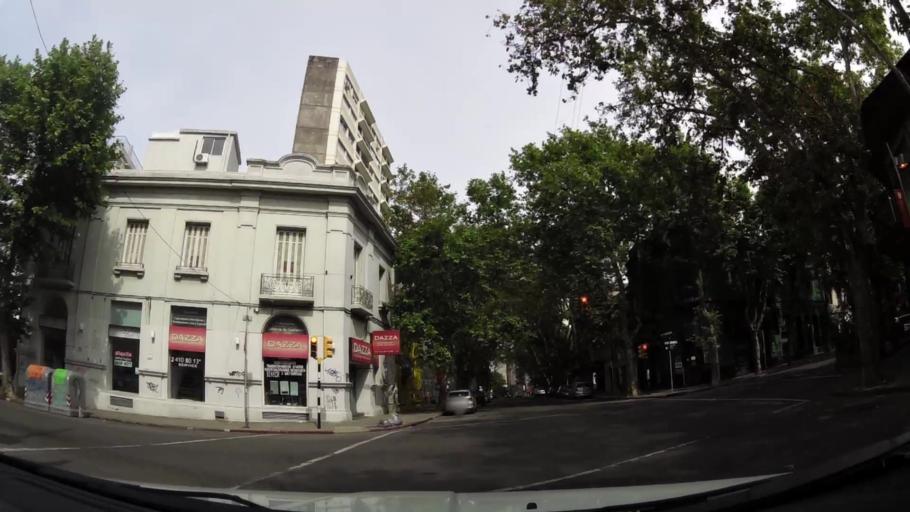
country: UY
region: Montevideo
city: Montevideo
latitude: -34.9081
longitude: -56.1718
